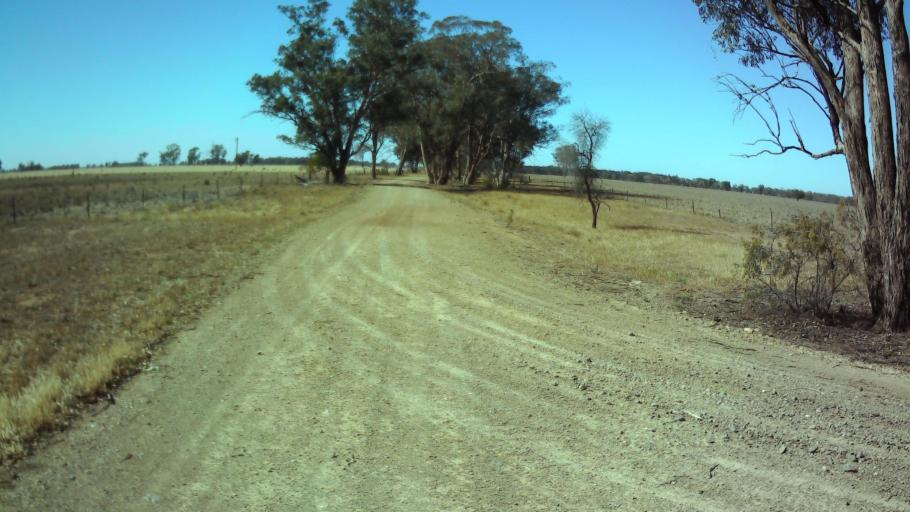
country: AU
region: New South Wales
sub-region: Weddin
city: Grenfell
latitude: -33.9452
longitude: 147.8702
